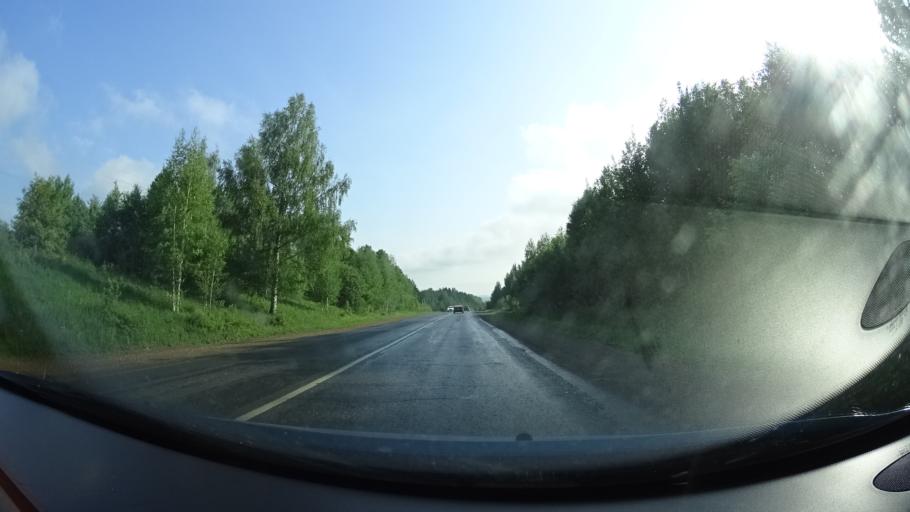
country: RU
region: Perm
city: Kultayevo
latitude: 57.8412
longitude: 55.8256
